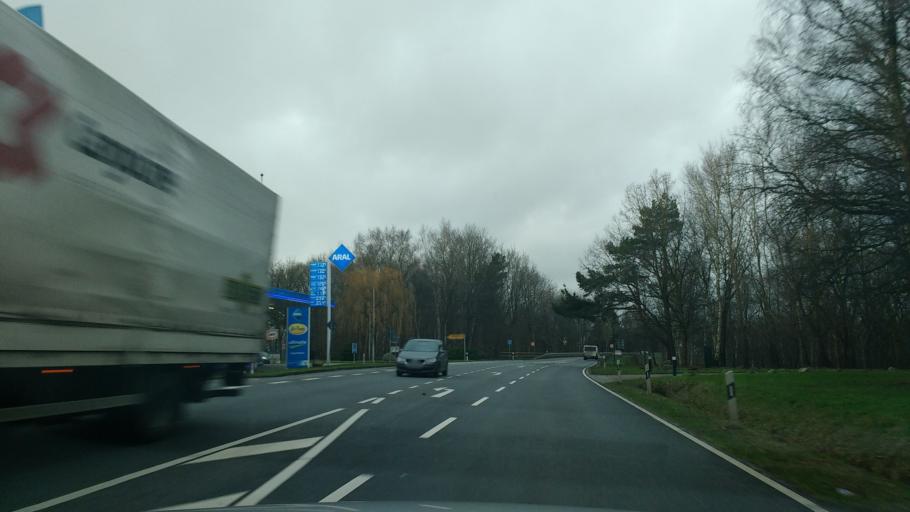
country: DE
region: Schleswig-Holstein
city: Itzehoe
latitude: 53.9054
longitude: 9.5085
